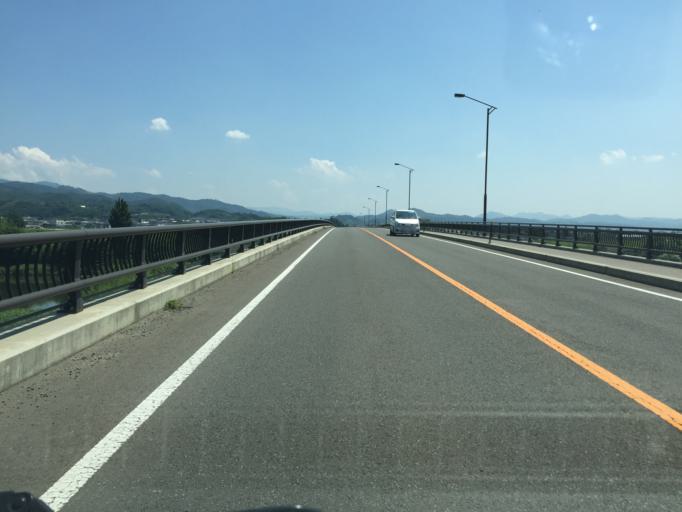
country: JP
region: Fukushima
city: Yanagawamachi-saiwaicho
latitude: 37.8703
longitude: 140.6084
